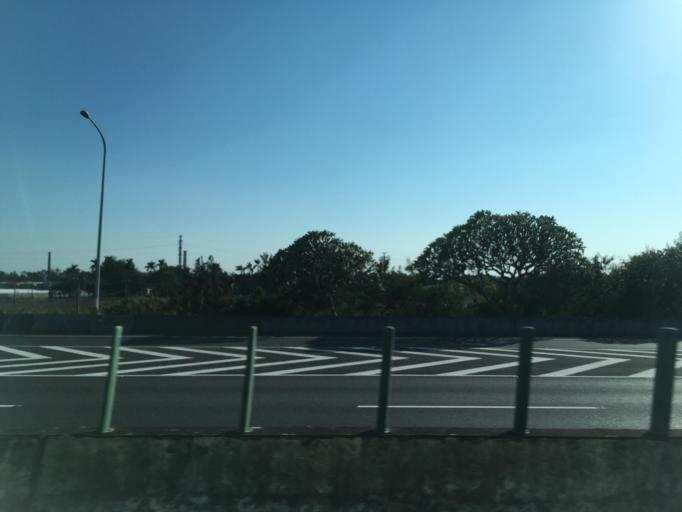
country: TW
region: Taiwan
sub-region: Chiayi
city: Taibao
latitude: 23.4197
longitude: 120.3807
